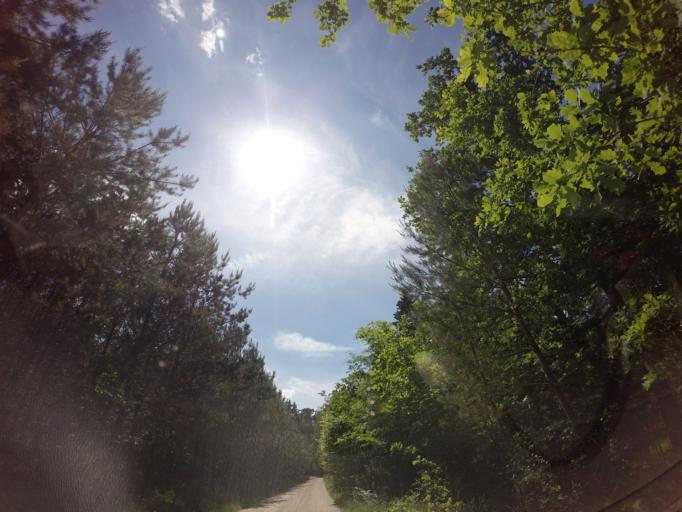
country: PL
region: West Pomeranian Voivodeship
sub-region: Powiat choszczenski
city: Drawno
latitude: 53.2269
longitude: 15.8182
